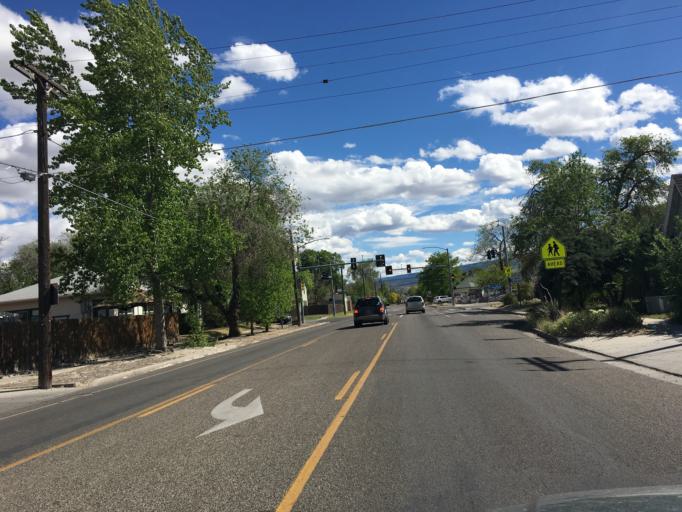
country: US
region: Colorado
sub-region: Mesa County
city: Grand Junction
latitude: 39.0711
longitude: -108.5524
